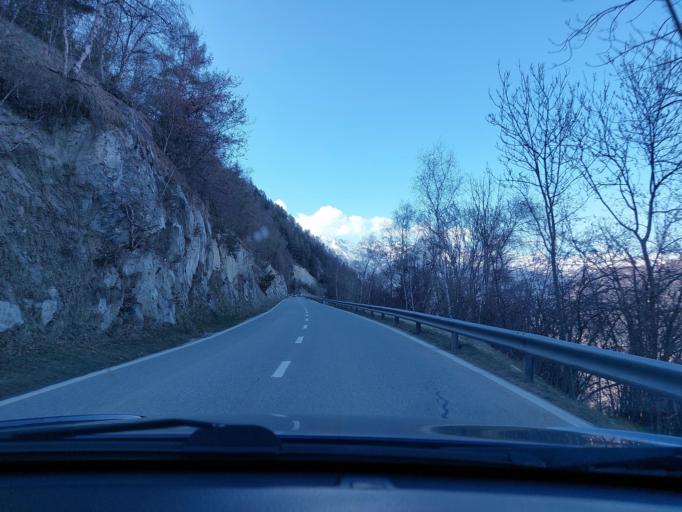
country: CH
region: Valais
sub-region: Herens District
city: Heremence
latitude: 46.1848
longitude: 7.4102
